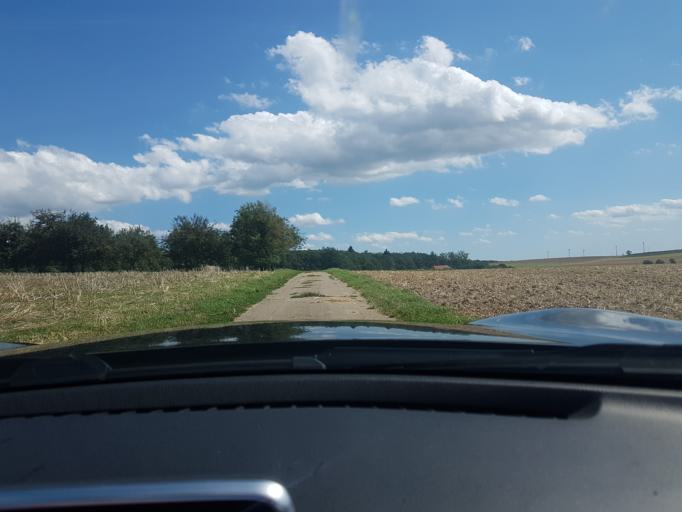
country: DE
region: Baden-Wuerttemberg
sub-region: Regierungsbezirk Stuttgart
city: Widdern
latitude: 49.3412
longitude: 9.3961
